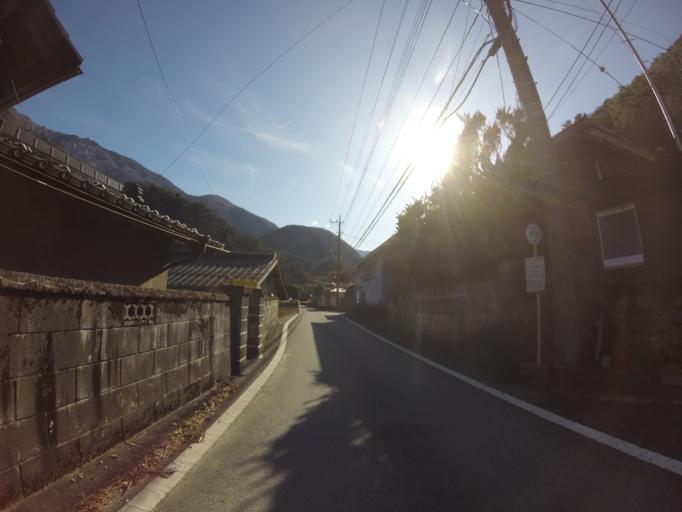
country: JP
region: Yamanashi
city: Ryuo
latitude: 35.3955
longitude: 138.3227
